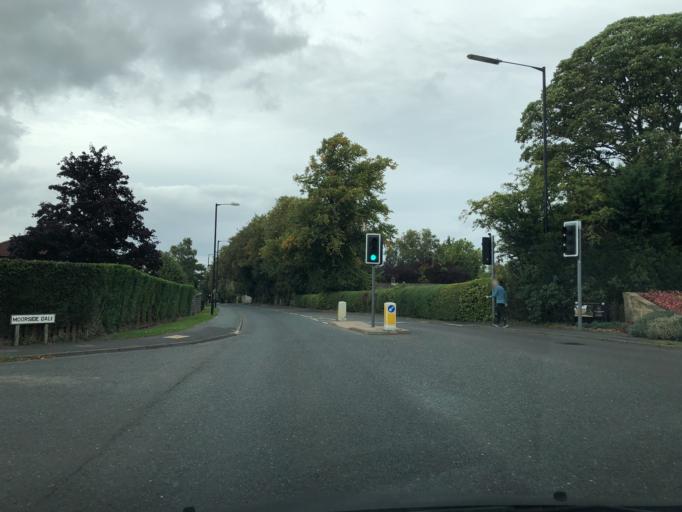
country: GB
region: England
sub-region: North Yorkshire
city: Ripon
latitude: 54.1227
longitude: -1.5256
